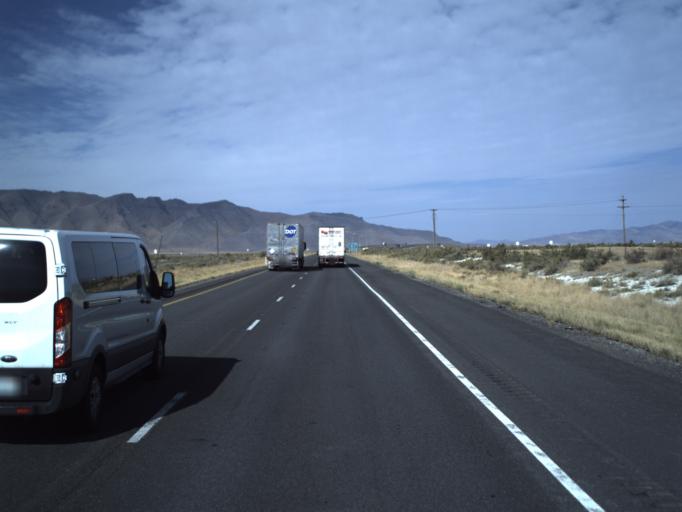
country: US
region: Utah
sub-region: Tooele County
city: Grantsville
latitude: 40.7054
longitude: -112.5126
